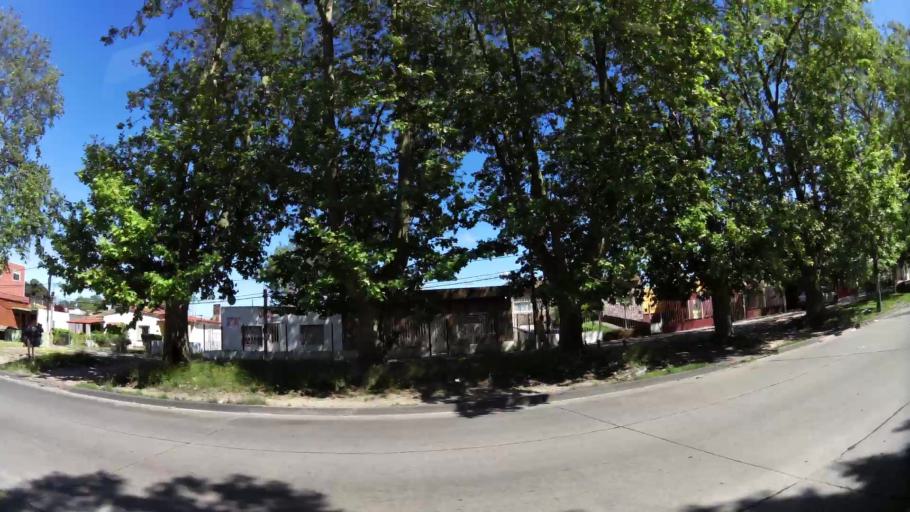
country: UY
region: Canelones
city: Paso de Carrasco
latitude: -34.8507
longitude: -56.1281
